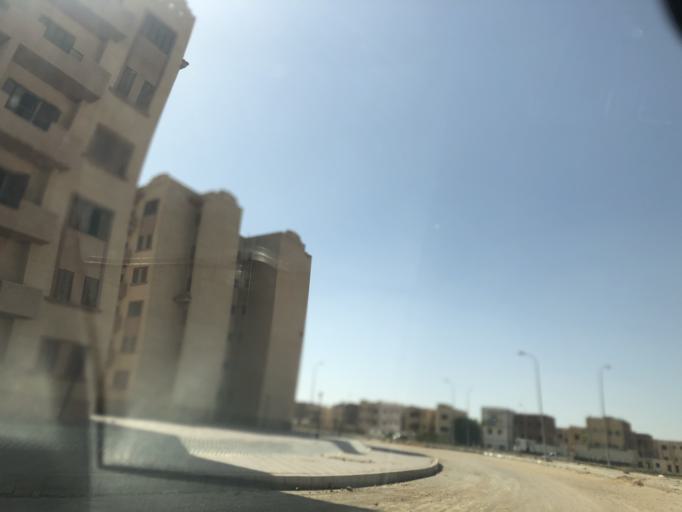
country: EG
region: Al Jizah
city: Madinat Sittah Uktubar
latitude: 29.9275
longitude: 31.0368
